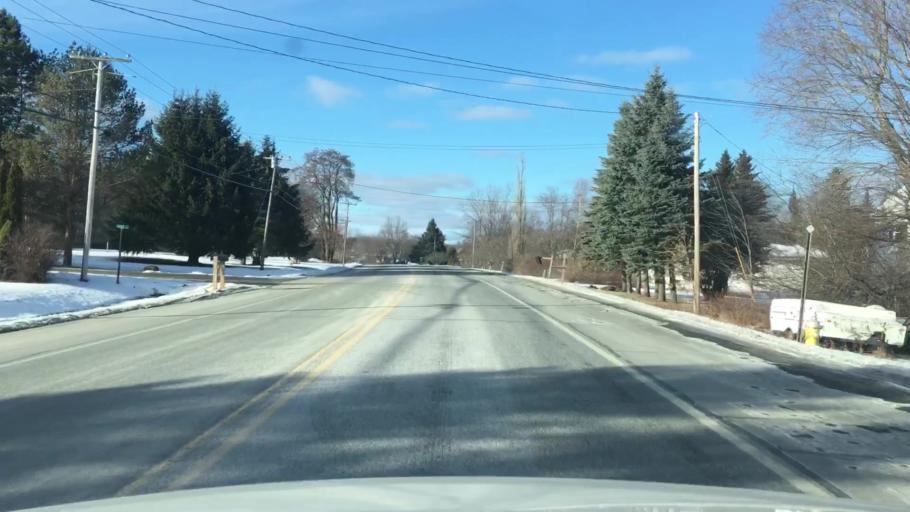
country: US
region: Maine
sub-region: Penobscot County
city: Eddington
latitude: 44.8212
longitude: -68.6491
